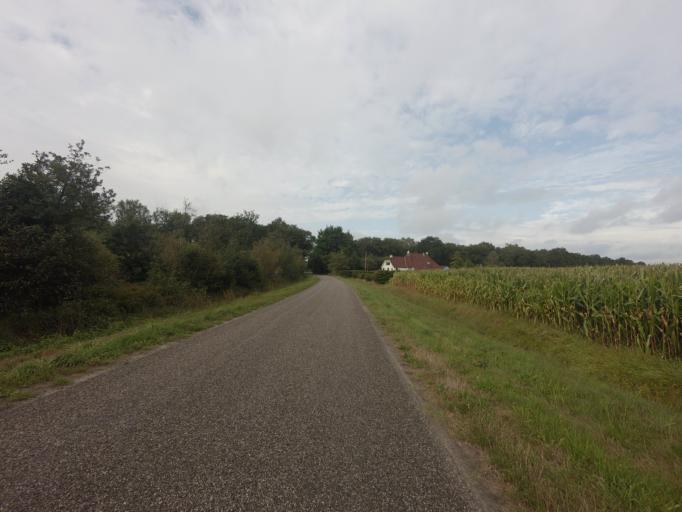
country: NL
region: Friesland
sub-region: Gemeente Heerenveen
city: Jubbega
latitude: 52.9695
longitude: 6.1684
